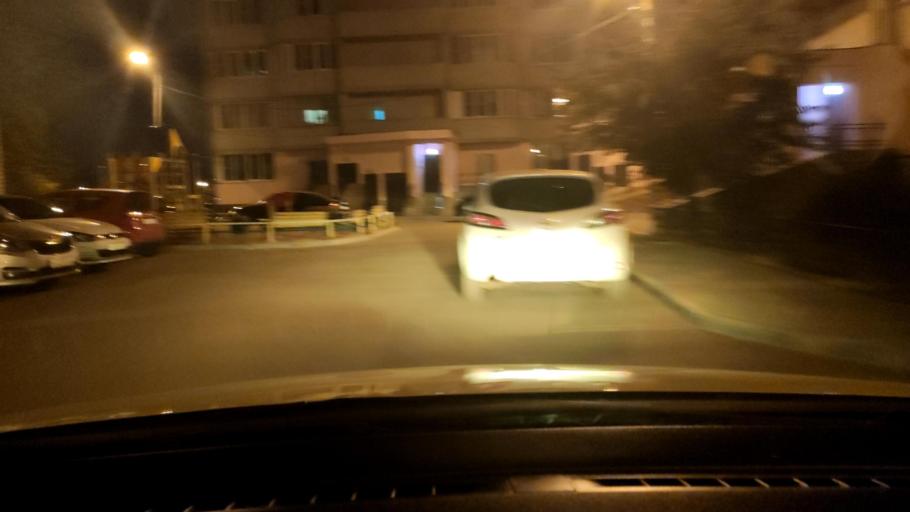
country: RU
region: Voronezj
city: Voronezh
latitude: 51.6870
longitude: 39.1991
